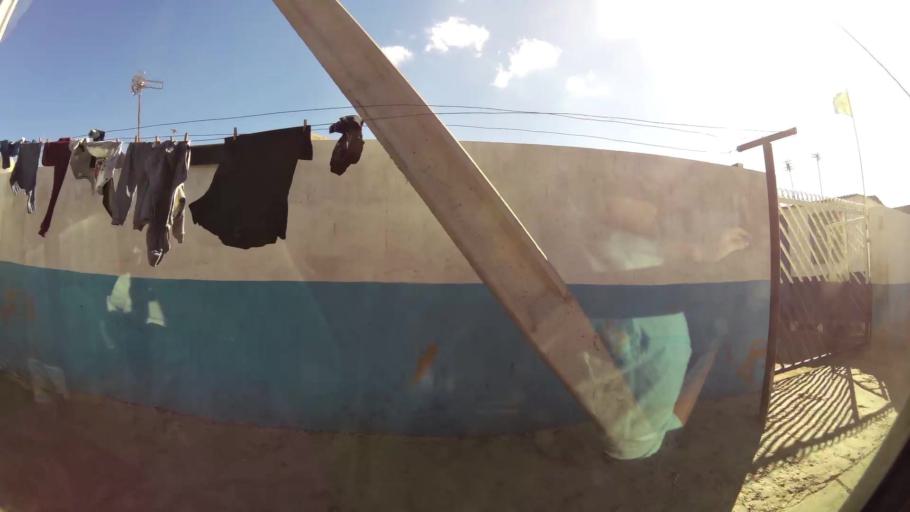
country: ZA
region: Gauteng
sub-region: Ekurhuleni Metropolitan Municipality
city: Tembisa
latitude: -26.0347
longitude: 28.1872
